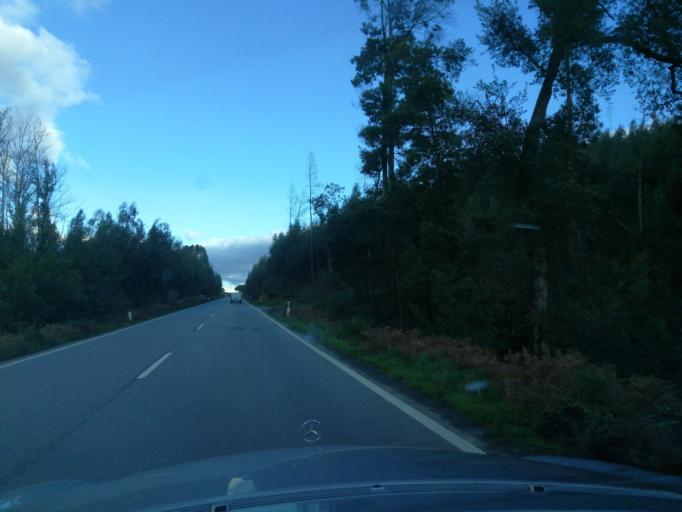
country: PT
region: Braga
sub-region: Barcelos
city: Vila Frescainha
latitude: 41.5728
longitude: -8.7054
